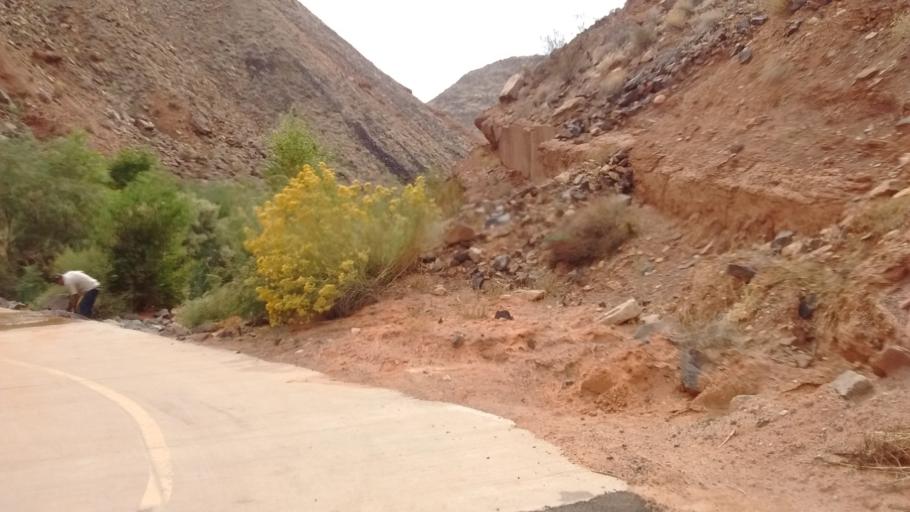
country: US
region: Utah
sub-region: Washington County
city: Washington
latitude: 37.1266
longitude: -113.4837
